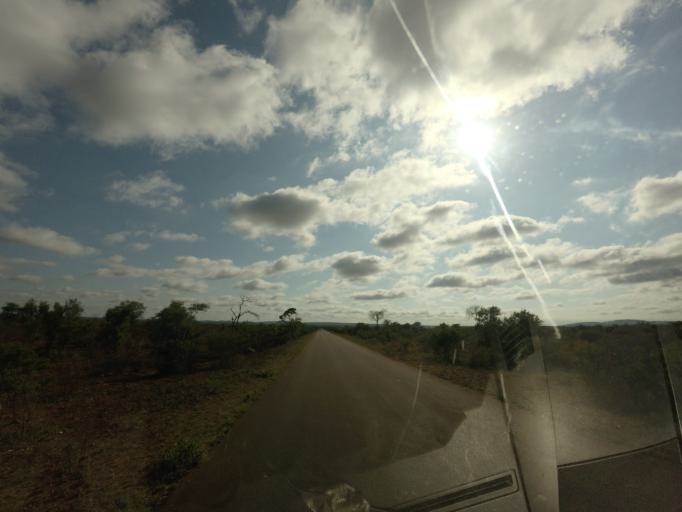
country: ZA
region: Mpumalanga
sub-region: Ehlanzeni District
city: Komatipoort
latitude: -25.1674
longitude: 31.9221
